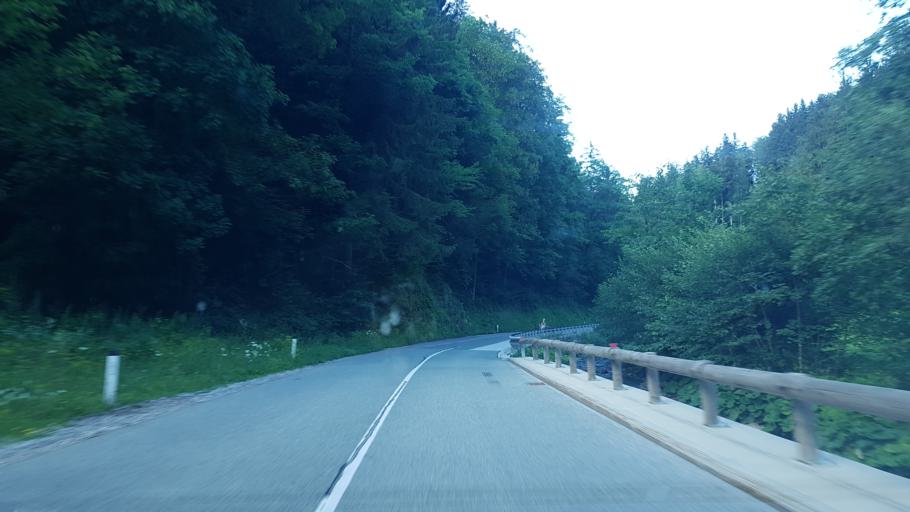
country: SI
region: Ziri
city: Ziri
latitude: 46.0813
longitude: 14.0780
